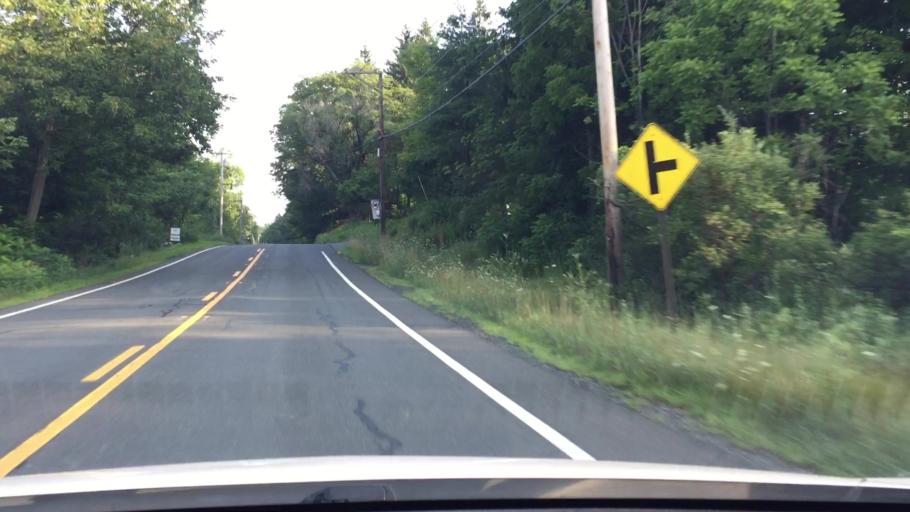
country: US
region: Massachusetts
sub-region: Berkshire County
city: Otis
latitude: 42.2355
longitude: -73.1123
